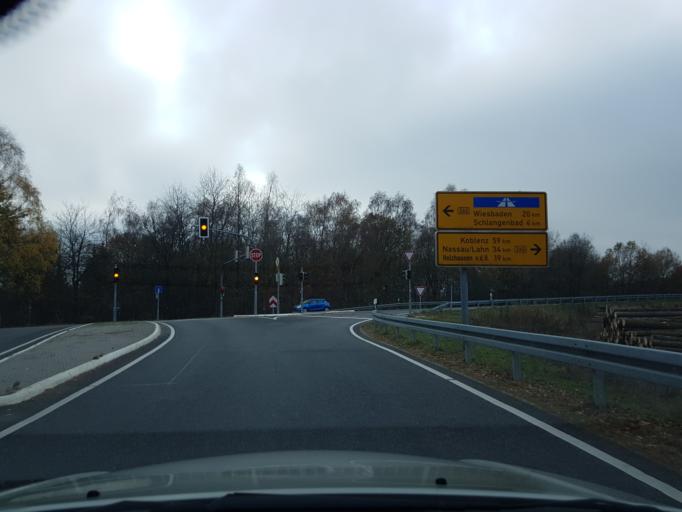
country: DE
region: Hesse
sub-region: Regierungsbezirk Darmstadt
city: Bad Schwalbach
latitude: 50.1191
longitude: 8.0808
